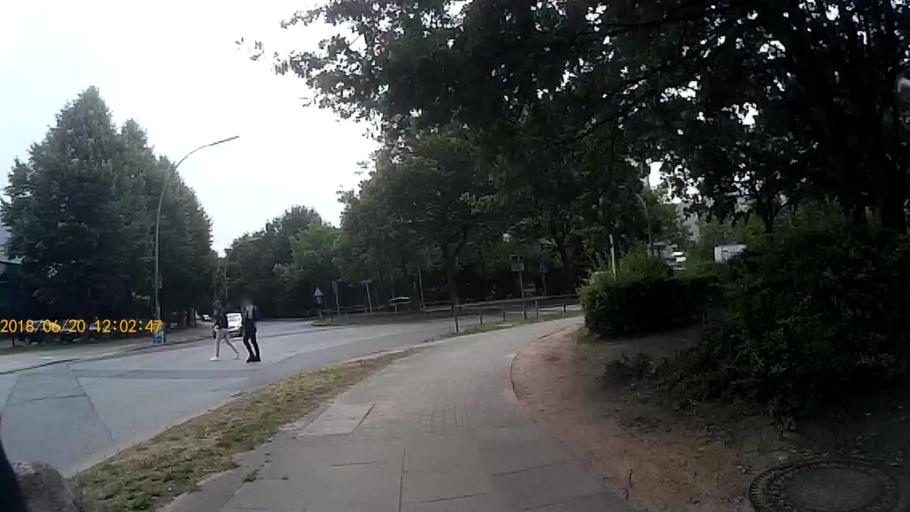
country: DE
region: Hamburg
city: Kleiner Grasbrook
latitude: 53.4979
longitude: 10.0127
